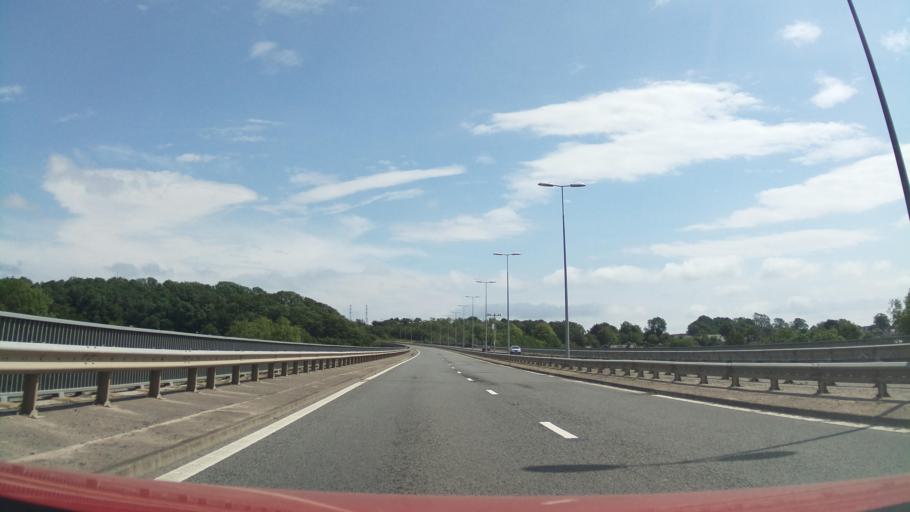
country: GB
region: Wales
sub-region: Vale of Glamorgan
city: Cowbridge
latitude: 51.4640
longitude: -3.4436
